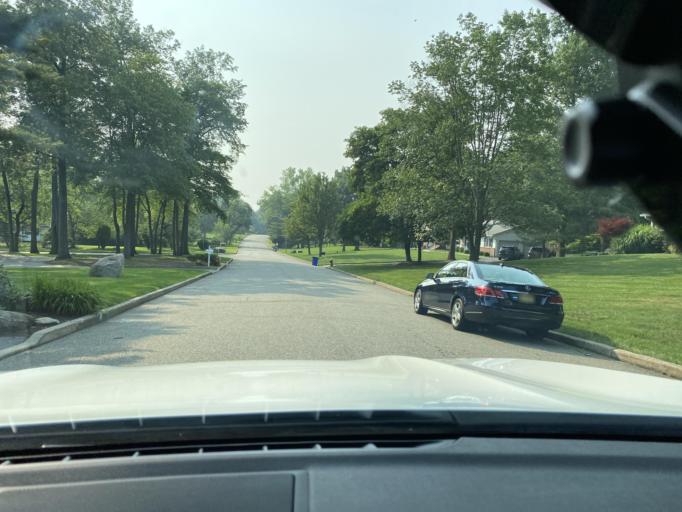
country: US
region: New York
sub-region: Rockland County
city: Airmont
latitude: 41.0925
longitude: -74.1179
